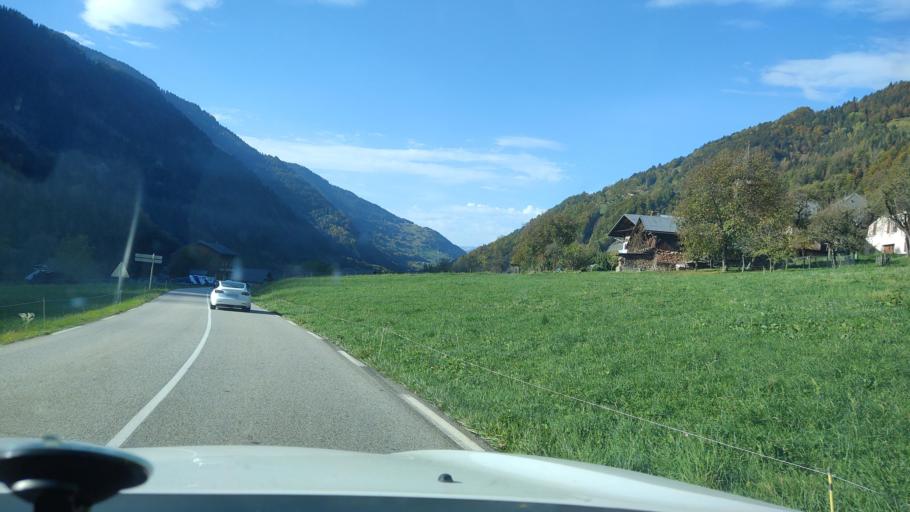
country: FR
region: Rhone-Alpes
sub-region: Departement de la Savoie
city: Beaufort
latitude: 45.7260
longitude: 6.5304
